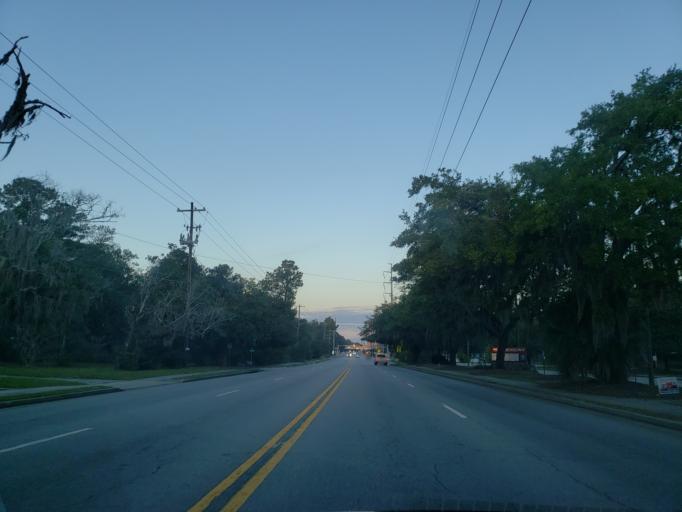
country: US
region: Georgia
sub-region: Chatham County
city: Thunderbolt
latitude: 32.0212
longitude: -81.0825
